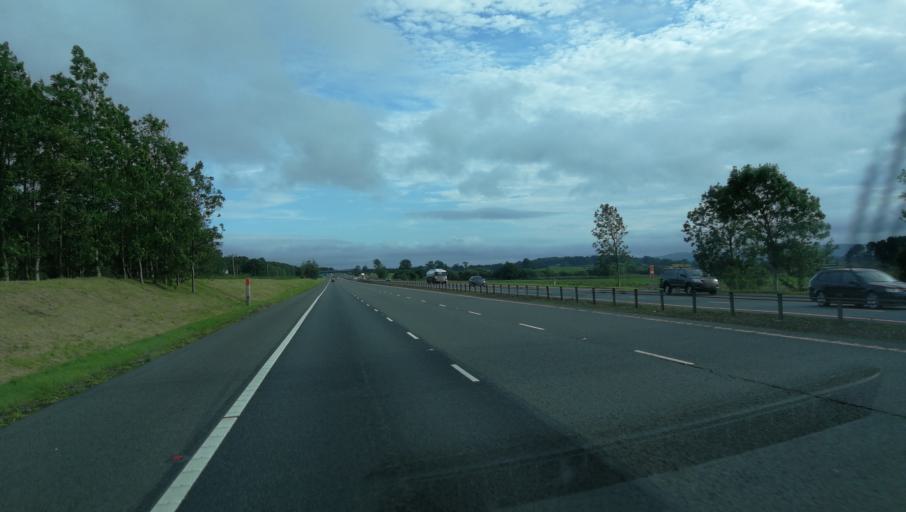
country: GB
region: Scotland
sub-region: Dumfries and Galloway
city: Lockerbie
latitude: 55.1601
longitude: -3.3859
